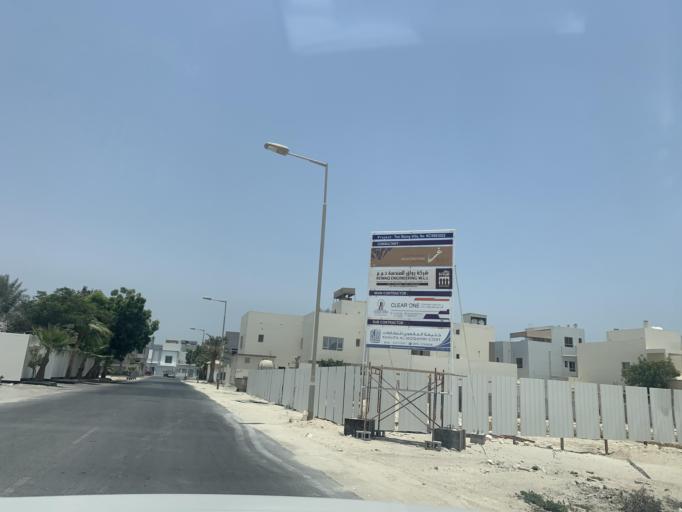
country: BH
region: Manama
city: Jidd Hafs
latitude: 26.2095
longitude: 50.4698
